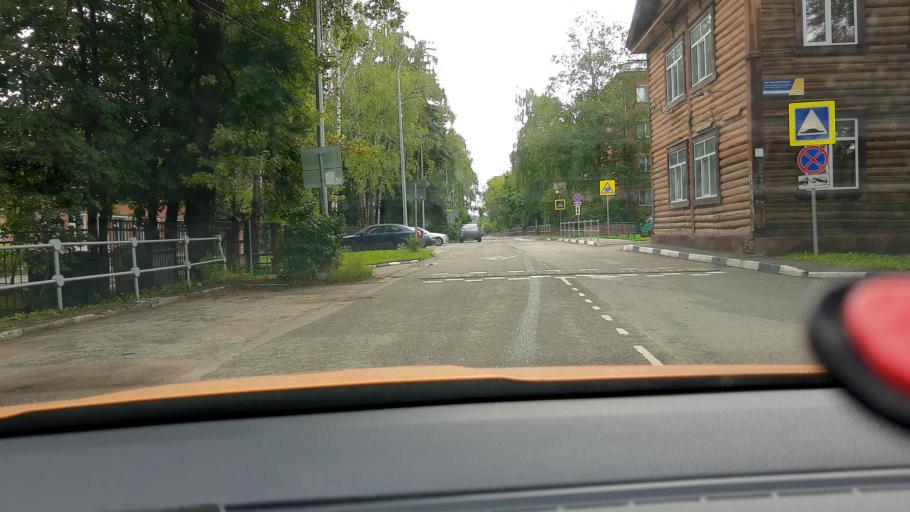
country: RU
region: Moskovskaya
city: Gorki Vtoryye
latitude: 55.7256
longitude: 37.1614
